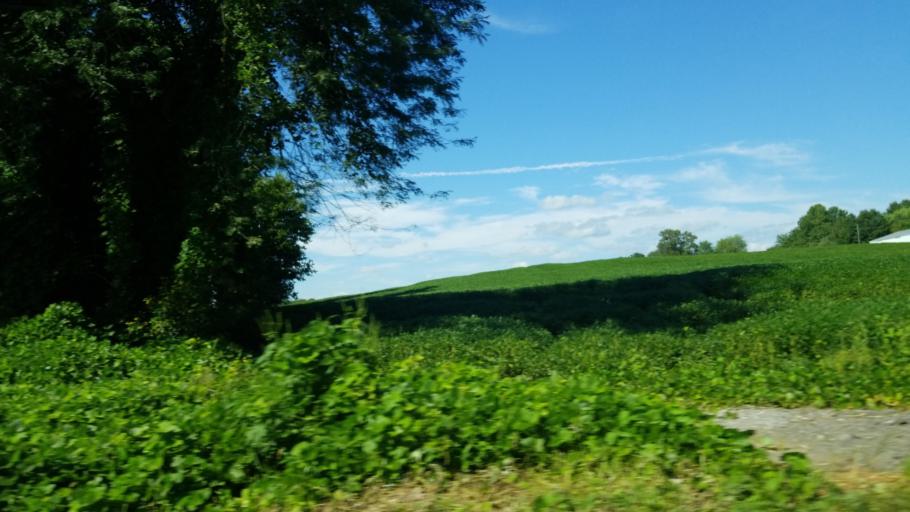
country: US
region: Illinois
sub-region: Saline County
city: Carrier Mills
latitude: 37.7977
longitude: -88.7452
